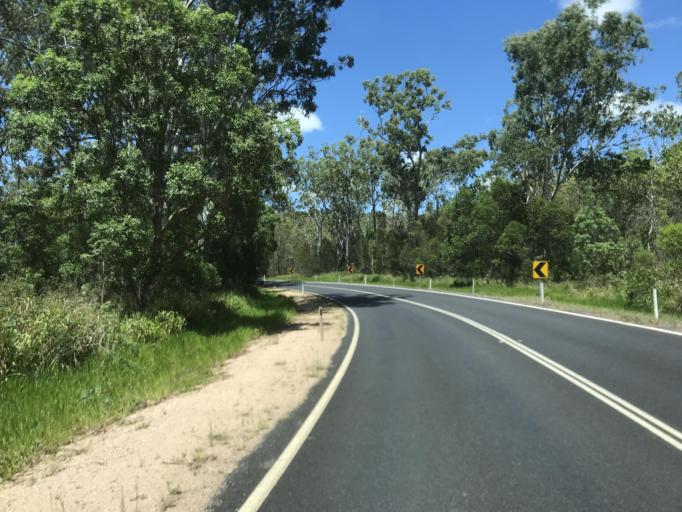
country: AU
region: Queensland
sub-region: Tablelands
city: Atherton
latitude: -17.4038
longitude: 145.3896
